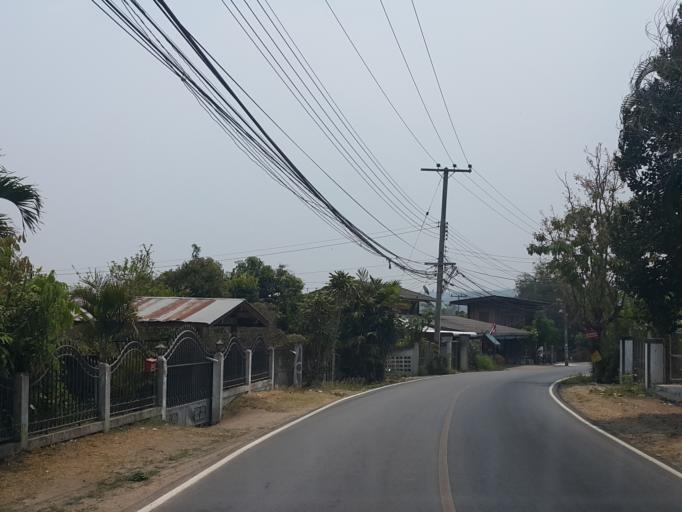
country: TH
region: Chiang Mai
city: Mae Taeng
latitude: 19.0214
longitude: 98.8760
